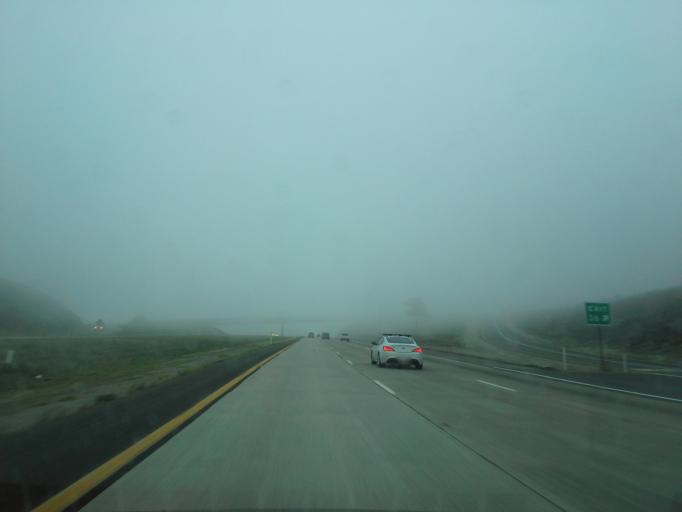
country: US
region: California
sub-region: San Diego County
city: Descanso
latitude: 32.8382
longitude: -116.6851
